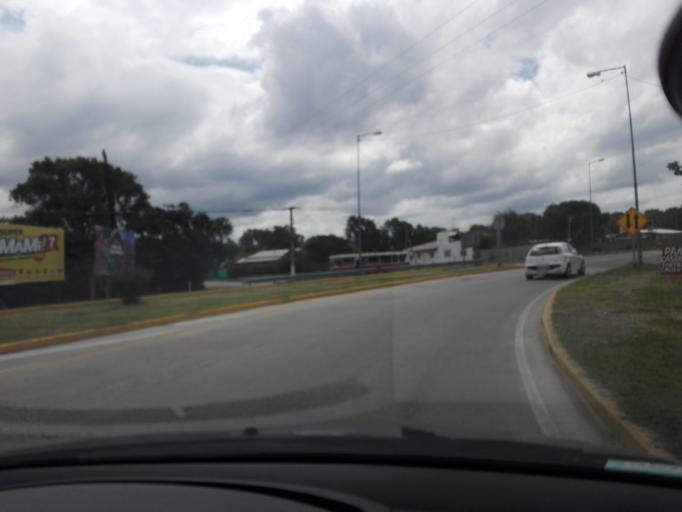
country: AR
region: Cordoba
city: Alta Gracia
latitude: -31.6347
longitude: -64.4355
